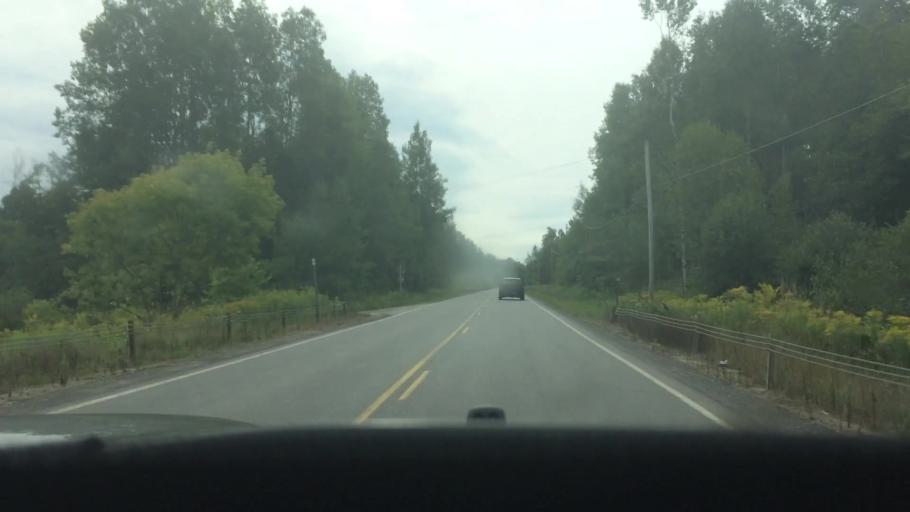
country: US
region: New York
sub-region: St. Lawrence County
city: Canton
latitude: 44.4837
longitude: -75.2473
